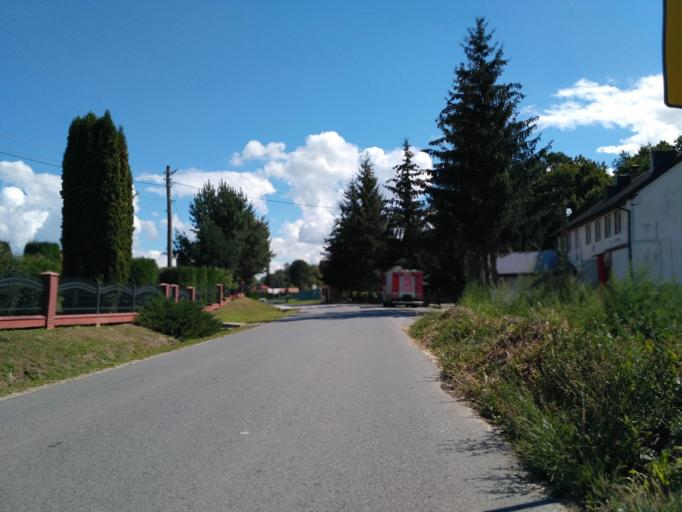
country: PL
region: Subcarpathian Voivodeship
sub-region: Powiat jasielski
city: Skolyszyn
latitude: 49.7916
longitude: 21.3306
